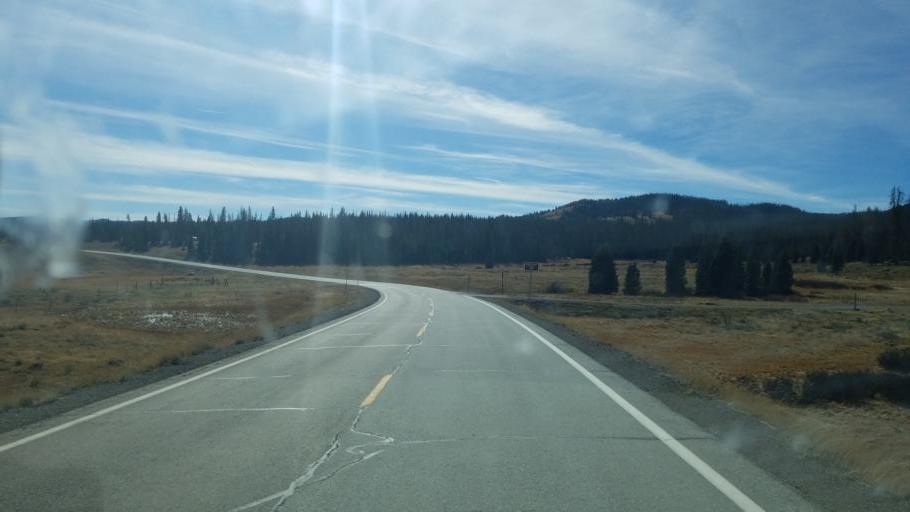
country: US
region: New Mexico
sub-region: Rio Arriba County
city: Chama
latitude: 37.0738
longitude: -106.3954
